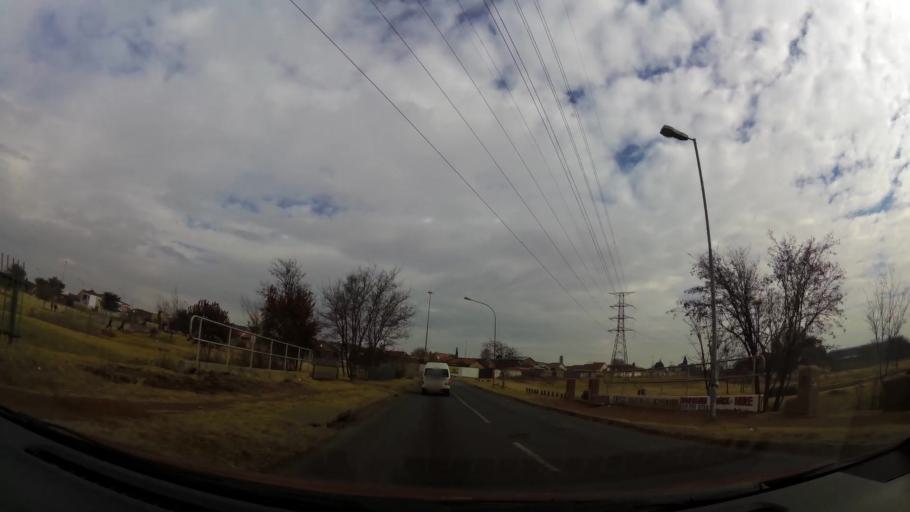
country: ZA
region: Gauteng
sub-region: City of Johannesburg Metropolitan Municipality
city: Soweto
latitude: -26.2719
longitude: 27.8383
